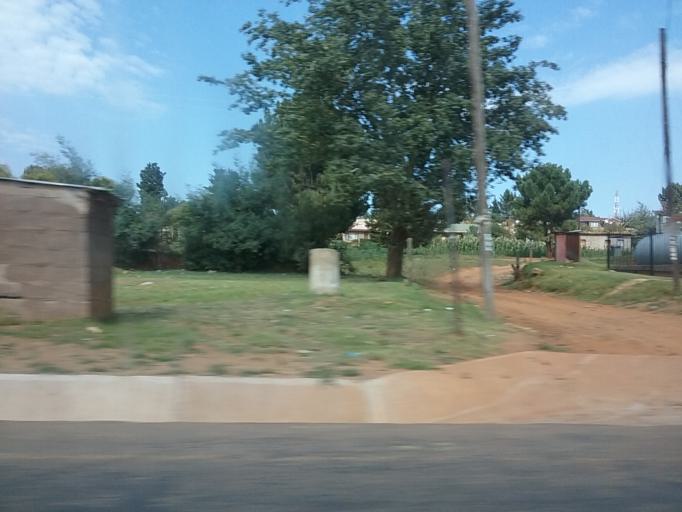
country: LS
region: Berea
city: Teyateyaneng
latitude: -29.1207
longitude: 27.9762
